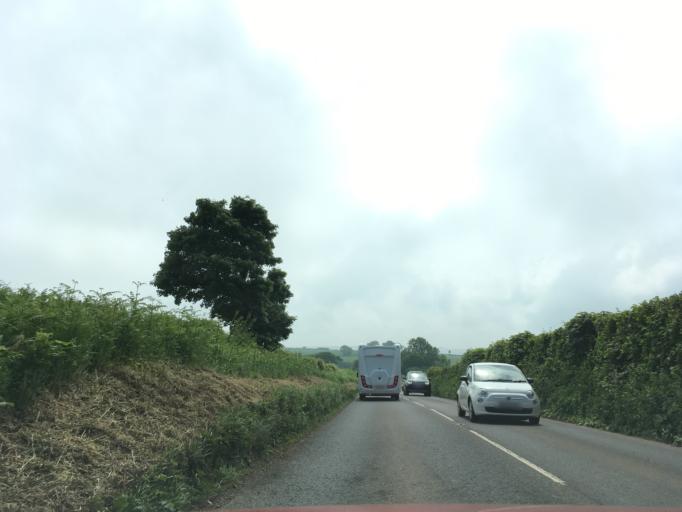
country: GB
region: England
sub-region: Devon
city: Totnes
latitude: 50.4155
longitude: -3.7063
